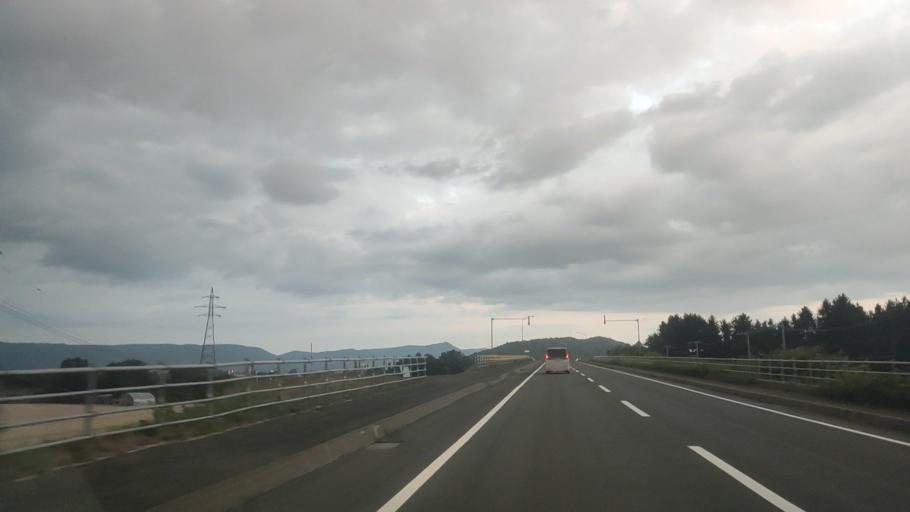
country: JP
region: Hokkaido
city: Shimo-furano
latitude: 43.3552
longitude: 142.3643
